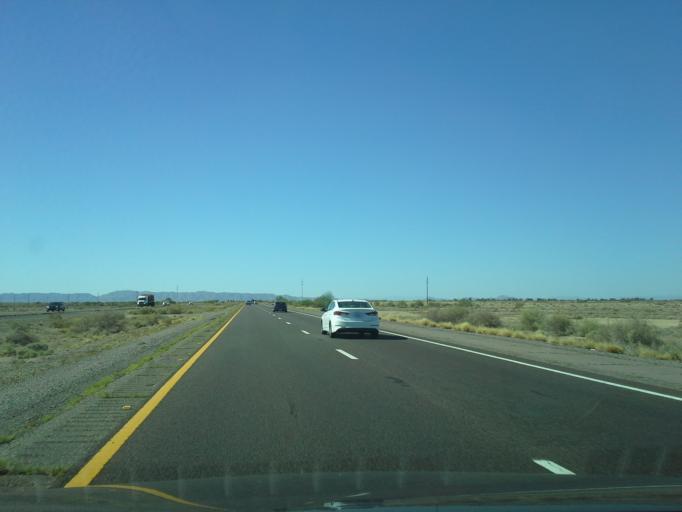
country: US
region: Arizona
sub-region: Pinal County
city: Casa Blanca
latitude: 33.1633
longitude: -111.8768
